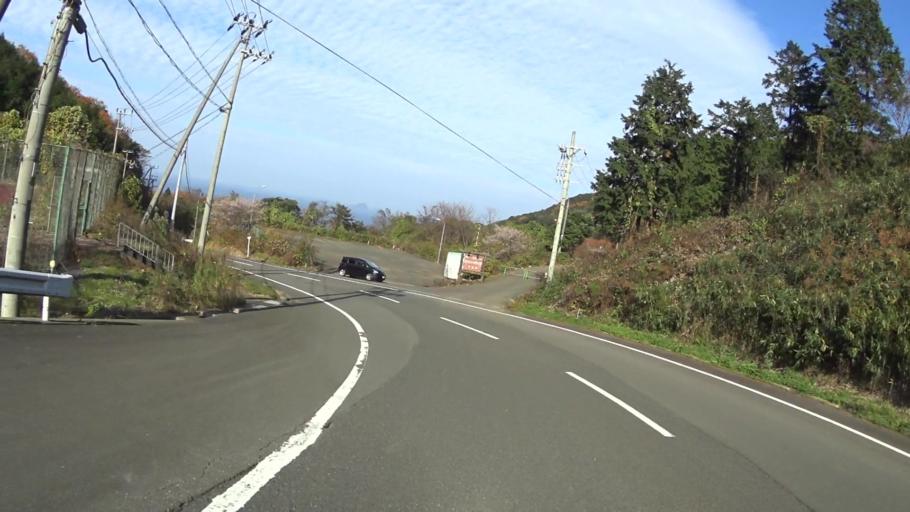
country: JP
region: Kyoto
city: Maizuru
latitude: 35.5406
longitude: 135.3973
